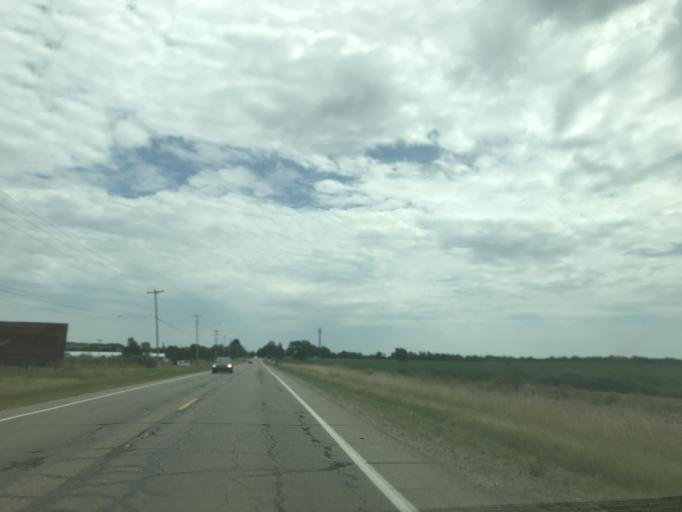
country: US
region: Michigan
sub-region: Clinton County
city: Wacousta
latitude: 42.7962
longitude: -84.7303
